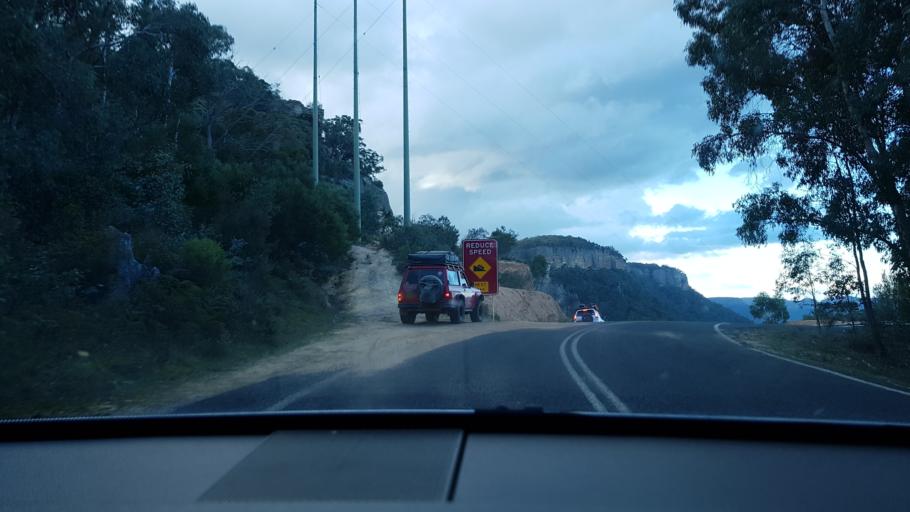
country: AU
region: New South Wales
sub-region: Lithgow
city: Portland
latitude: -33.3168
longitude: 150.1115
